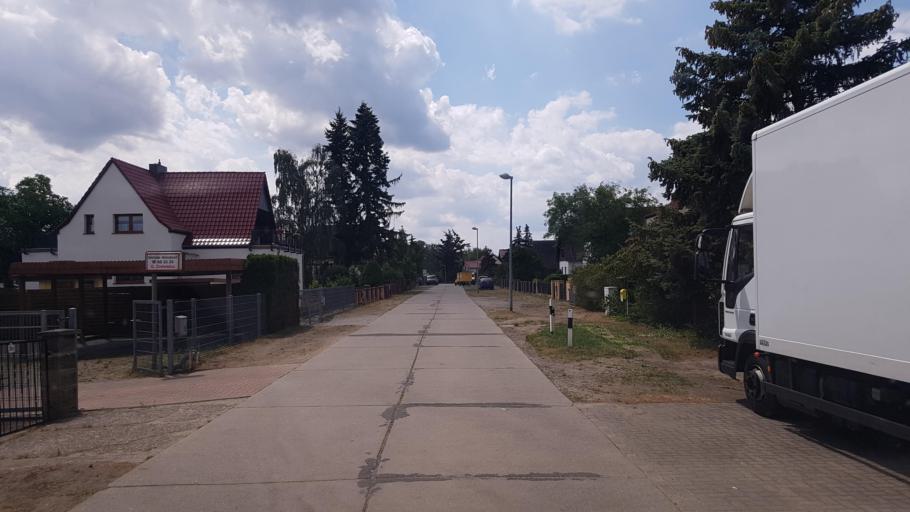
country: DE
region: Brandenburg
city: Brandenburg an der Havel
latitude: 52.3893
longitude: 12.5424
